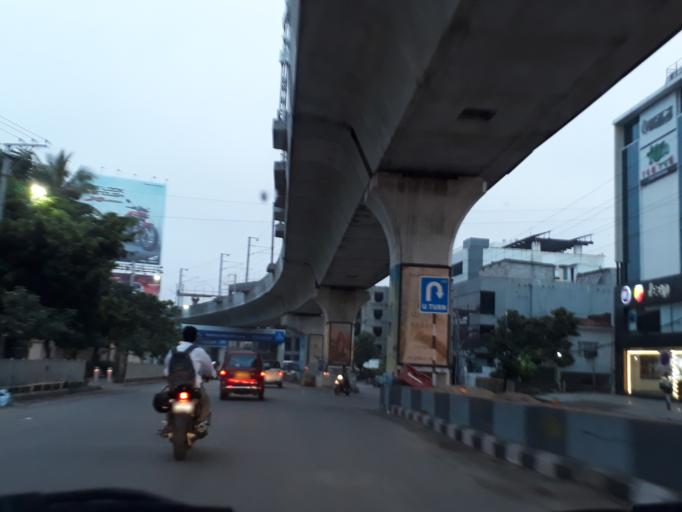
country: IN
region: Telangana
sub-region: Rangareddi
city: Kukatpalli
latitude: 17.4293
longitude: 78.4126
